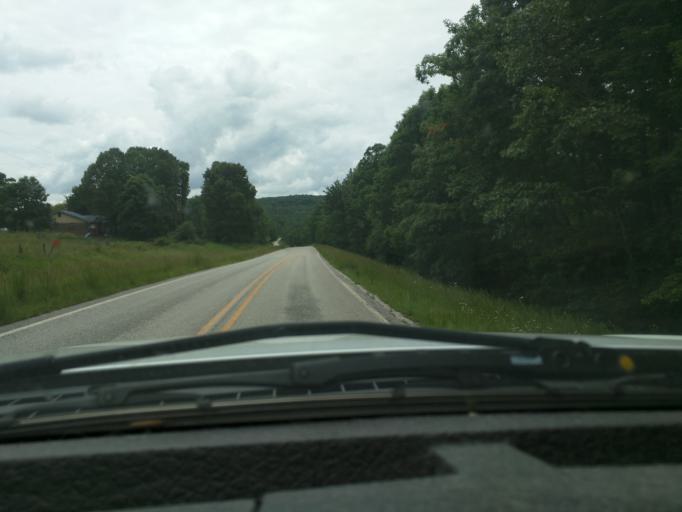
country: US
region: Arkansas
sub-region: Madison County
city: Huntsville
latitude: 35.8560
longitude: -93.5418
